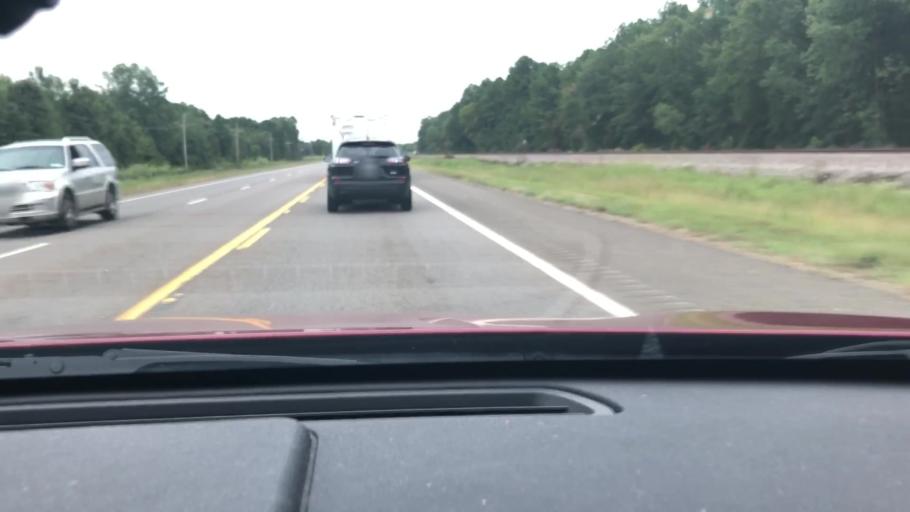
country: US
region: Arkansas
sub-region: Lafayette County
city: Lewisville
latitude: 33.3572
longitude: -93.5970
